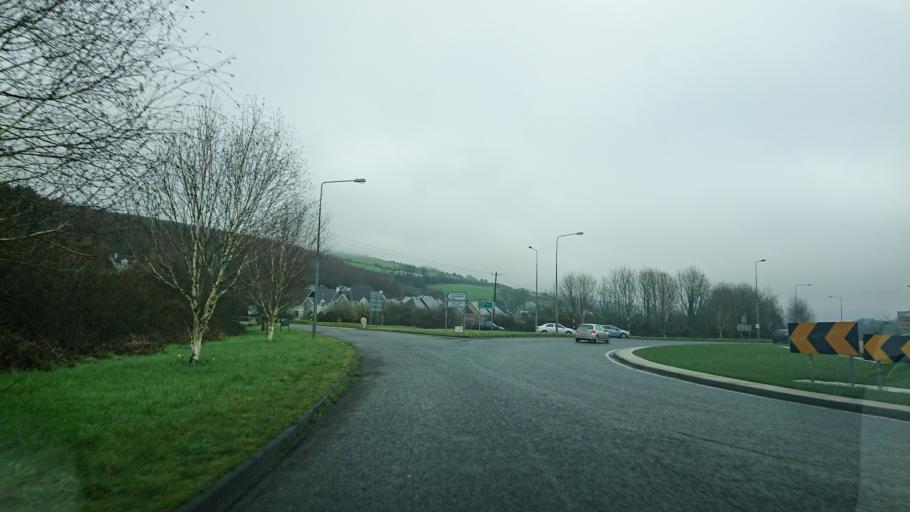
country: IE
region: Munster
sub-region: County Cork
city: Killumney
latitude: 51.8019
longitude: -8.5746
